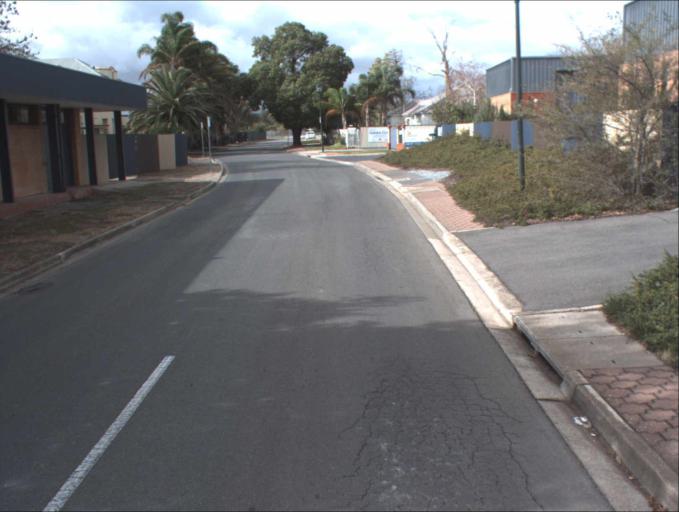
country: AU
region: South Australia
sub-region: Port Adelaide Enfield
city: Gilles Plains
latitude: -34.8513
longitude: 138.6379
